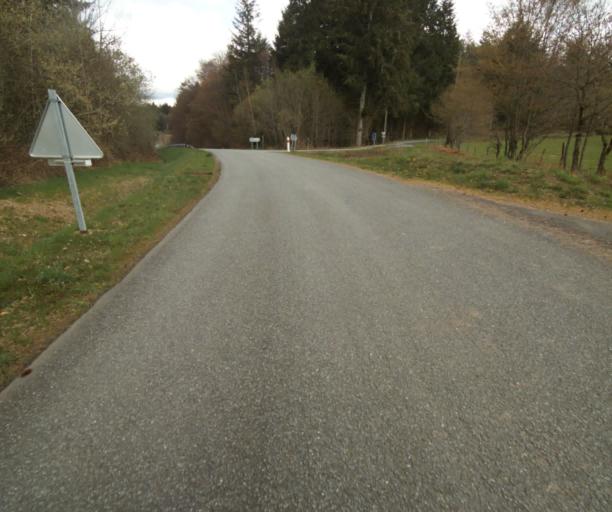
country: FR
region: Limousin
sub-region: Departement de la Correze
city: Correze
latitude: 45.3529
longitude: 1.9303
